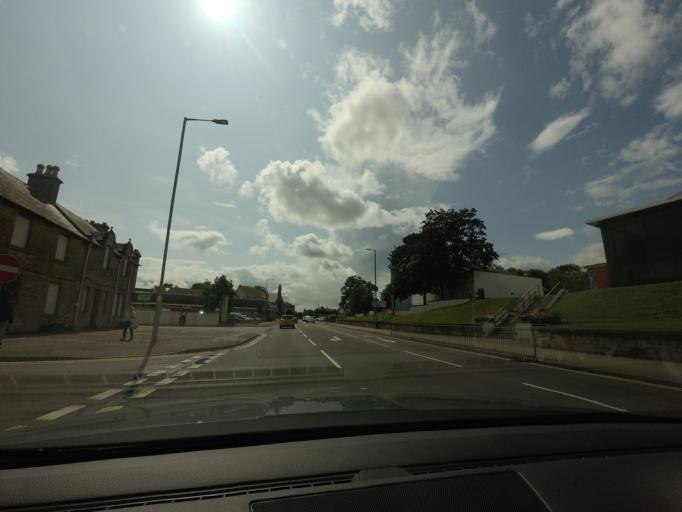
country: GB
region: Scotland
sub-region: Highland
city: Nairn
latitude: 57.5853
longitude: -3.8702
